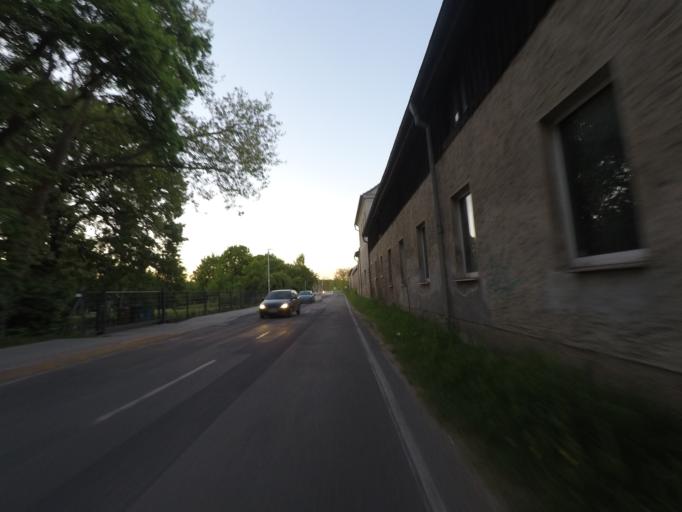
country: DE
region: Brandenburg
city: Melchow
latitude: 52.8487
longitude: 13.7265
